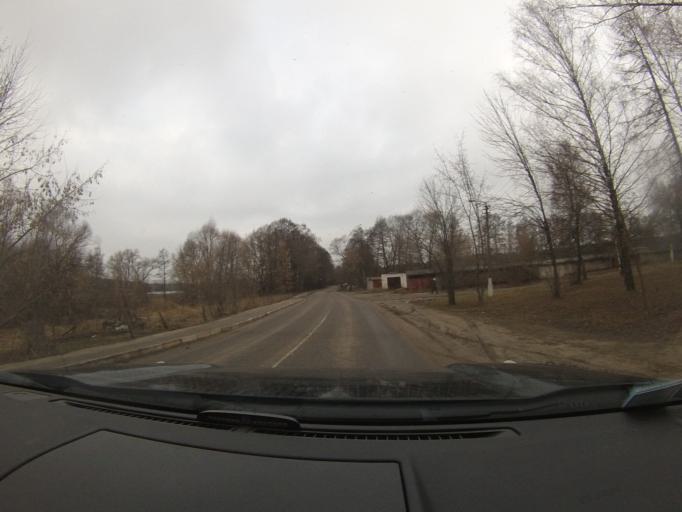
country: RU
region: Moskovskaya
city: Peski
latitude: 55.2619
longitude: 38.7623
